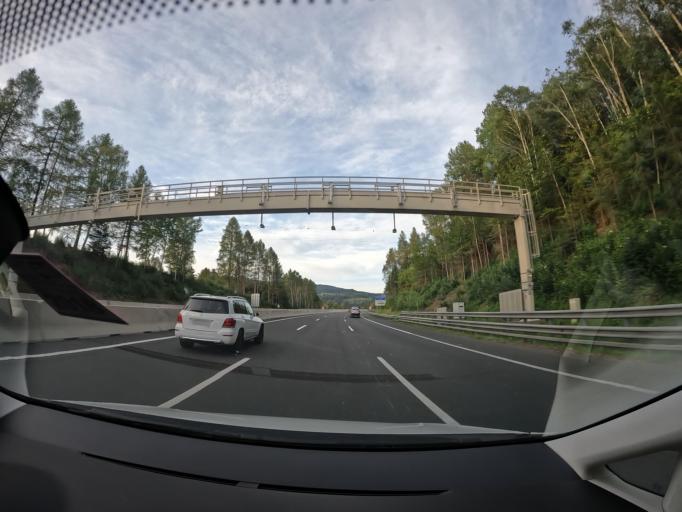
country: AT
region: Carinthia
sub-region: Politischer Bezirk Wolfsberg
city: Bad Sankt Leonhard im Lavanttal
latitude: 46.9373
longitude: 14.8294
